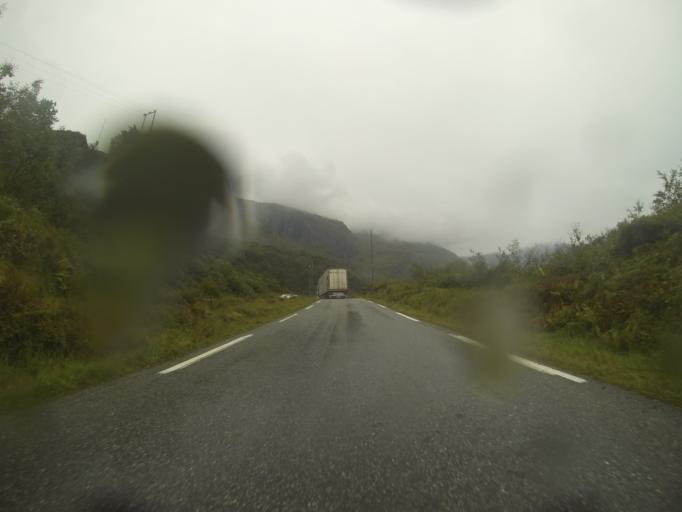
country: NO
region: Rogaland
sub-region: Sauda
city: Sauda
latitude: 59.7206
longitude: 6.5602
